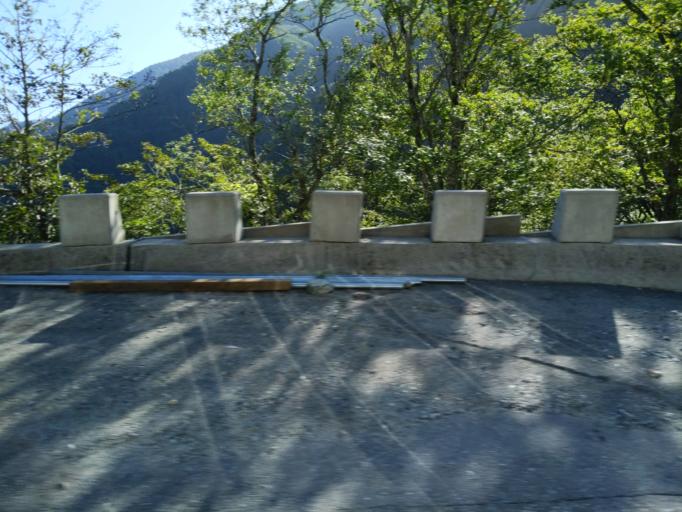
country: JP
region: Toyama
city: Kamiichi
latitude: 36.5079
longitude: 137.4489
